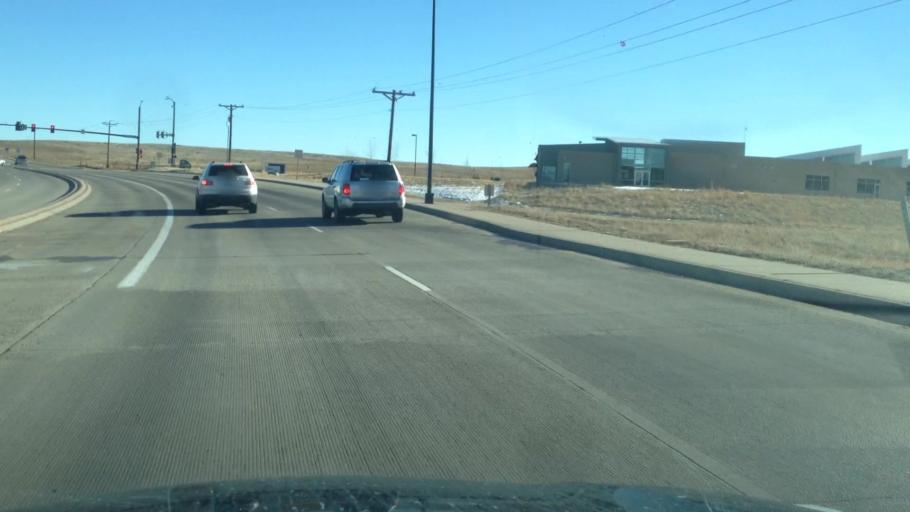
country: US
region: Colorado
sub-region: Arapahoe County
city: Dove Valley
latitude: 39.5831
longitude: -104.8143
